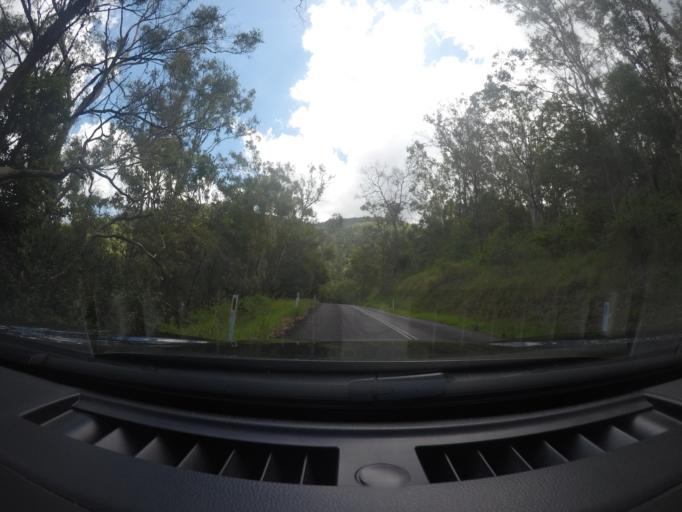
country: AU
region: Queensland
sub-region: Moreton Bay
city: Woodford
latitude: -27.1005
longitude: 152.5609
